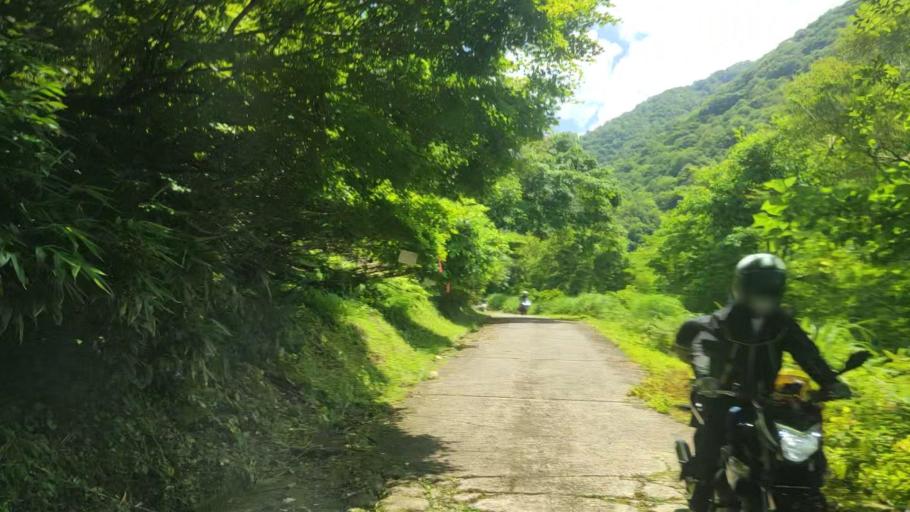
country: JP
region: Fukui
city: Ono
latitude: 35.7892
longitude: 136.5048
